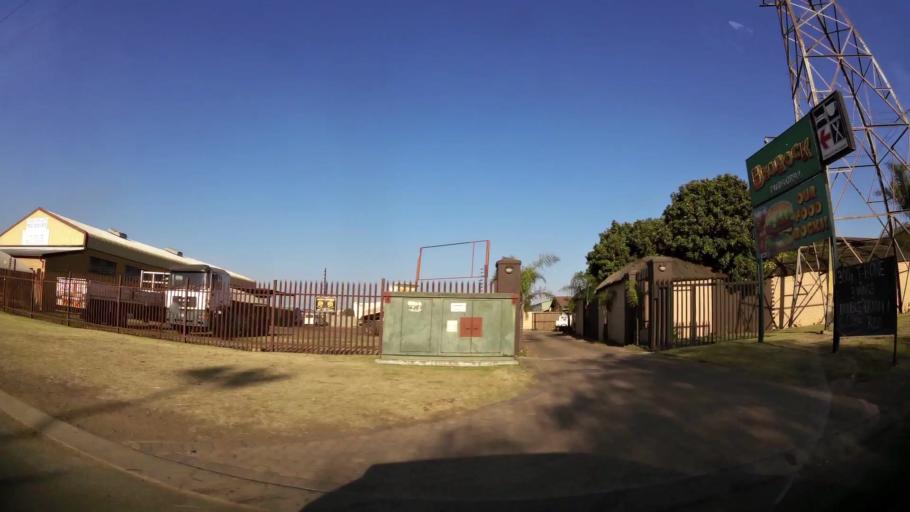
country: ZA
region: Gauteng
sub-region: West Rand District Municipality
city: Randfontein
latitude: -26.1930
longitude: 27.6924
